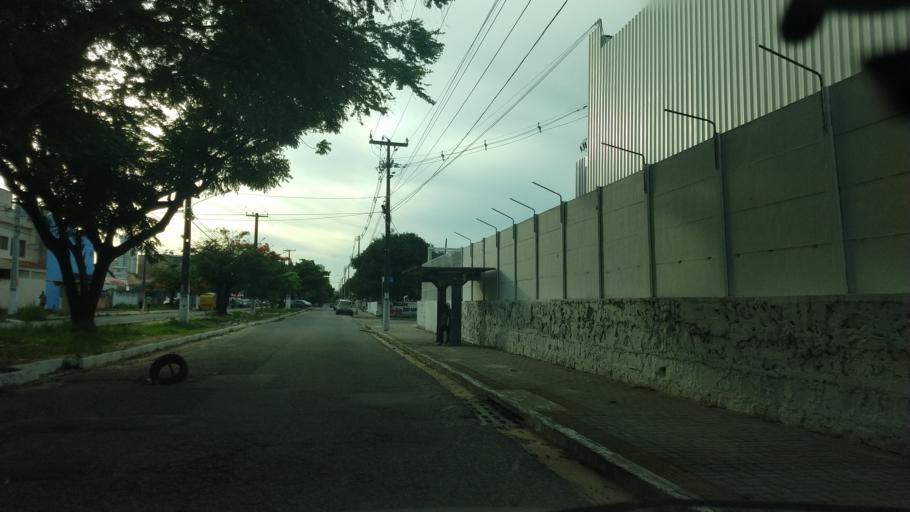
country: BR
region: Rio Grande do Norte
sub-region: Natal
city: Natal
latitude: -5.8306
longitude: -35.2080
